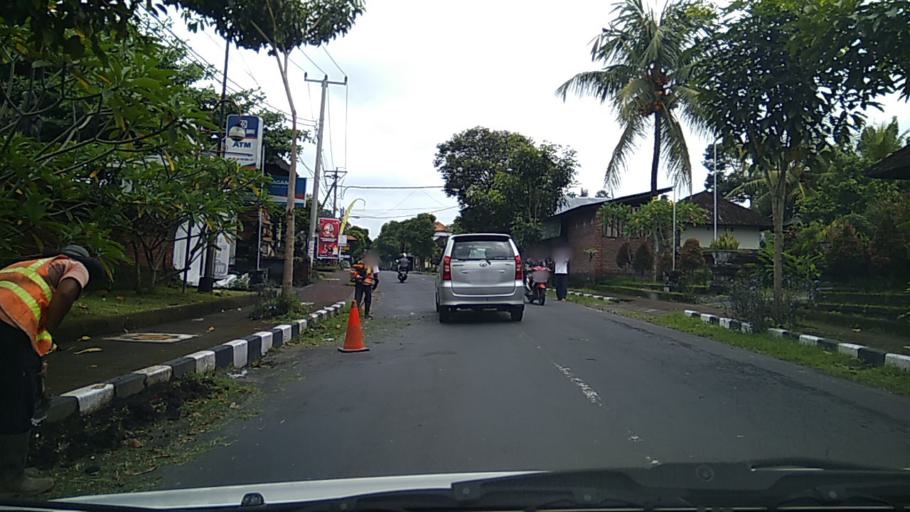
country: ID
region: Bali
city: Brahmana
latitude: -8.4855
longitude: 115.2103
